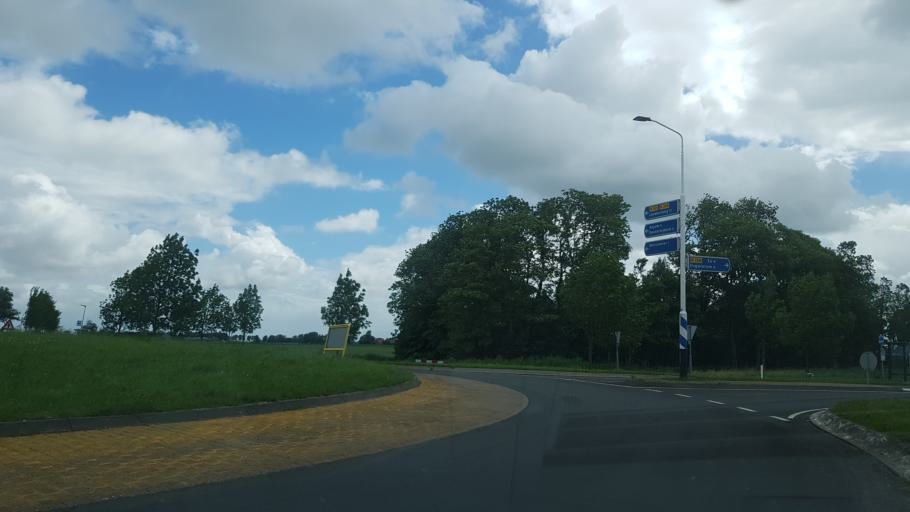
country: NL
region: Friesland
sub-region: Gemeente Dongeradeel
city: Anjum
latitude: 53.3580
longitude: 6.0752
